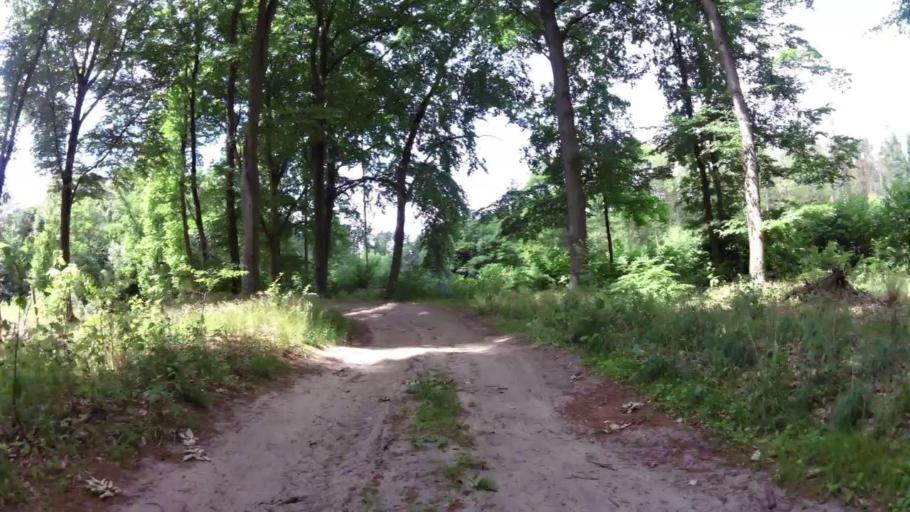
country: PL
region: West Pomeranian Voivodeship
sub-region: Powiat lobeski
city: Lobez
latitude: 53.5519
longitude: 15.6764
